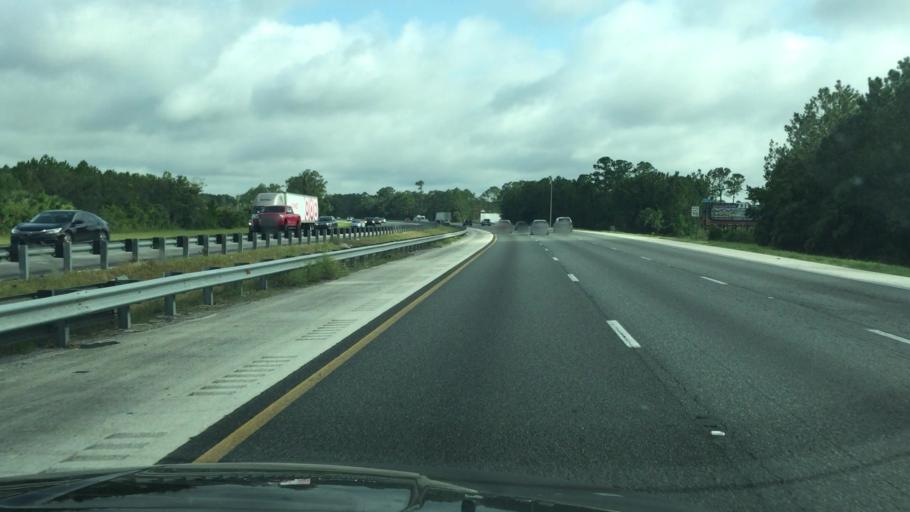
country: US
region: Florida
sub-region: Volusia County
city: Ormond-by-the-Sea
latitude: 29.3453
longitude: -81.1308
